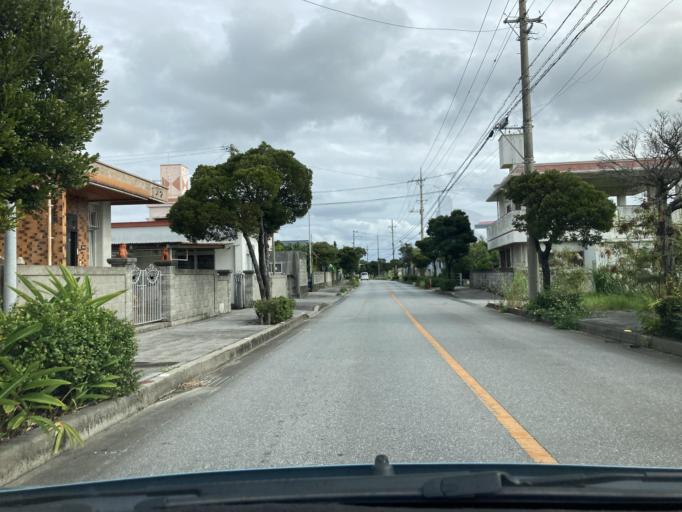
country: JP
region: Okinawa
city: Itoman
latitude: 26.1215
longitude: 127.6800
